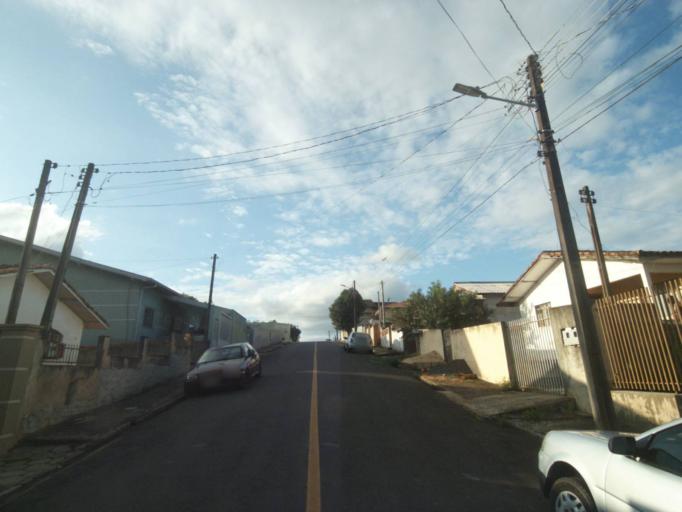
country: BR
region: Parana
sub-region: Telemaco Borba
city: Telemaco Borba
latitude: -24.3239
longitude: -50.6397
